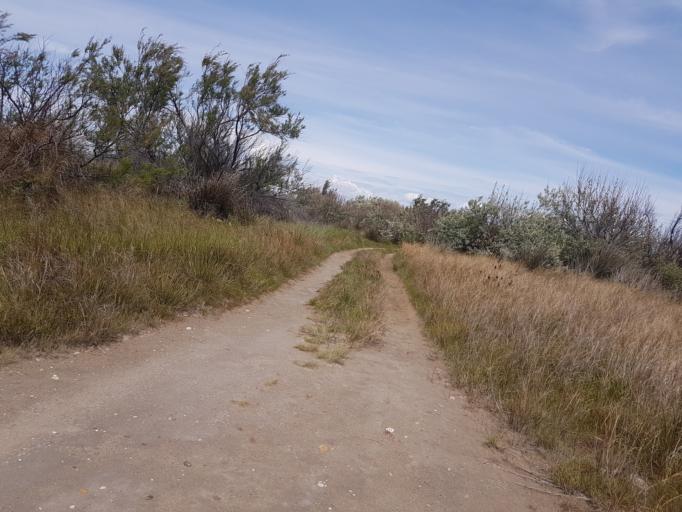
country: FR
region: Languedoc-Roussillon
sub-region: Departement de l'Herault
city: Vic-la-Gardiole
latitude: 43.4723
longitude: 3.8306
